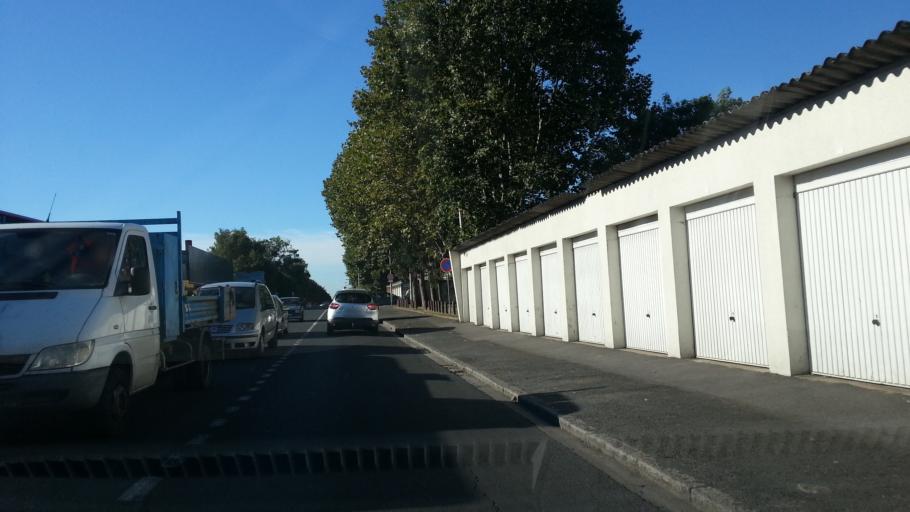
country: FR
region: Picardie
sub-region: Departement de l'Oise
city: Creil
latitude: 49.2521
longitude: 2.4770
